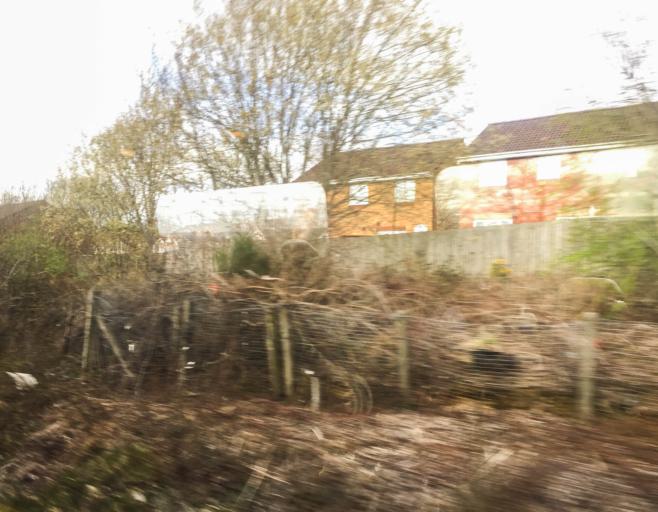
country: GB
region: Scotland
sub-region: North Lanarkshire
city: Wishaw
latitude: 55.7682
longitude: -3.9186
